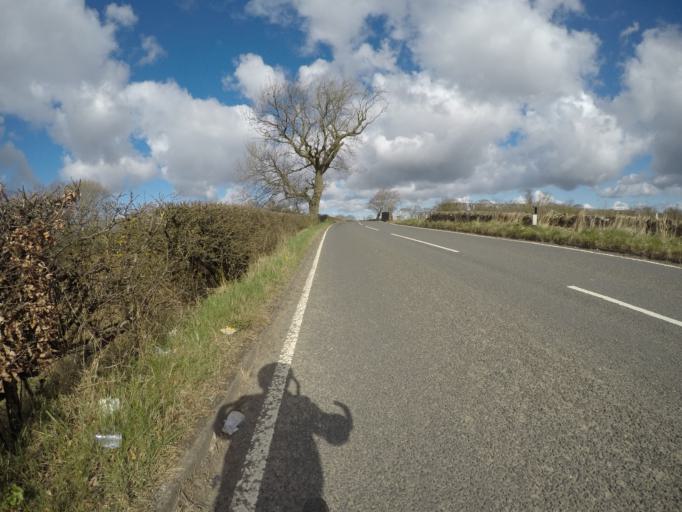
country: GB
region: Scotland
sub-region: North Ayrshire
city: Beith
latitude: 55.7355
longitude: -4.6171
